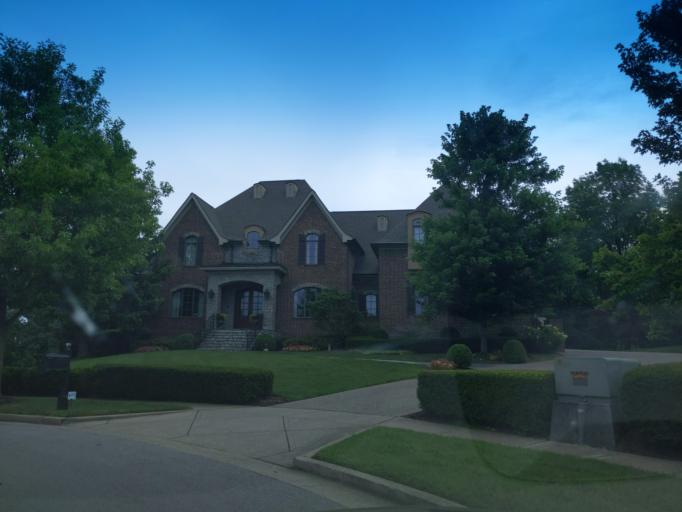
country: US
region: Tennessee
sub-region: Williamson County
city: Brentwood Estates
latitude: 36.0270
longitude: -86.7678
